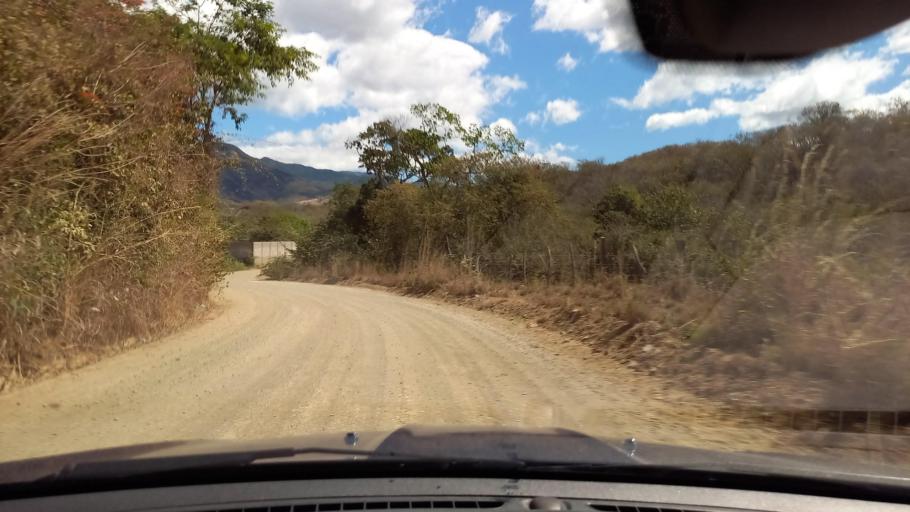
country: SV
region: Santa Ana
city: Metapan
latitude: 14.3608
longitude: -89.4628
